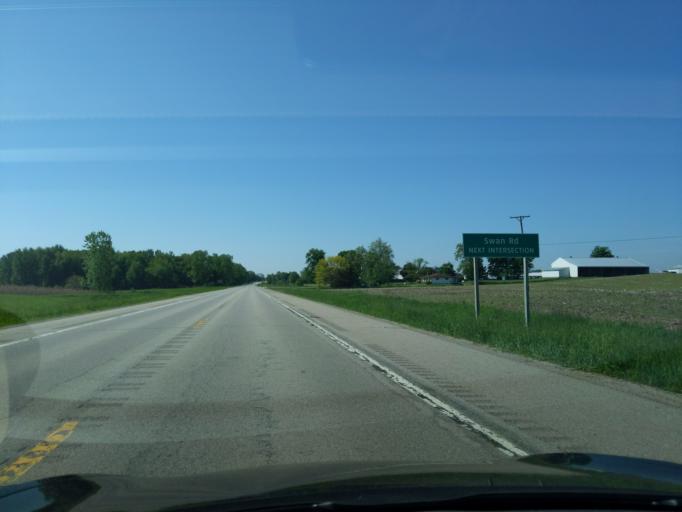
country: US
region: Michigan
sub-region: Ingham County
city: Stockbridge
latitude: 42.5209
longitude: -84.1904
